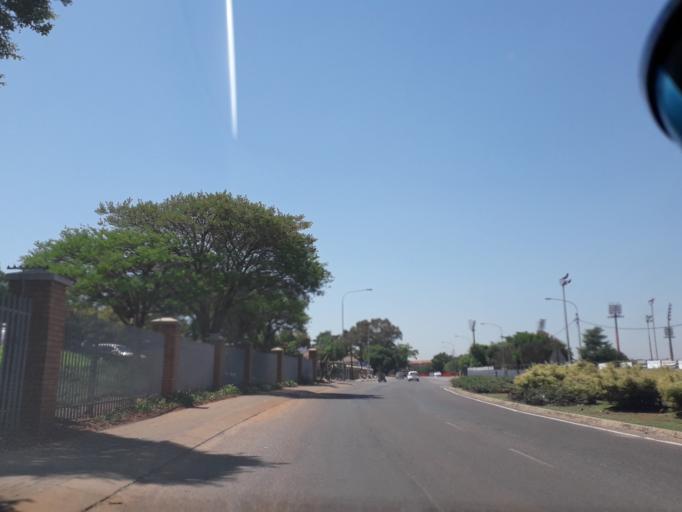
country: ZA
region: Gauteng
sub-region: City of Tshwane Metropolitan Municipality
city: Centurion
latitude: -25.8554
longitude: 28.1931
